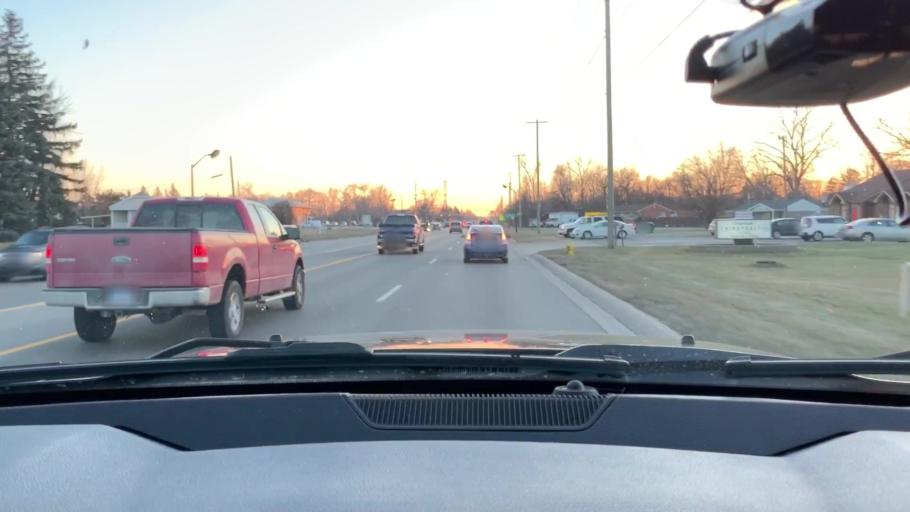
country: US
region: Michigan
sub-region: Wayne County
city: Flat Rock
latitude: 42.1260
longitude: -83.2744
